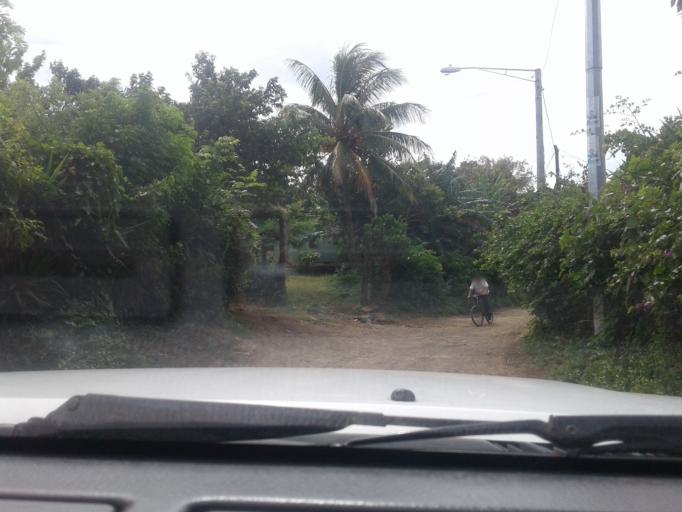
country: NI
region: Carazo
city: Diriamba
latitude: 11.8494
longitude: -86.2398
